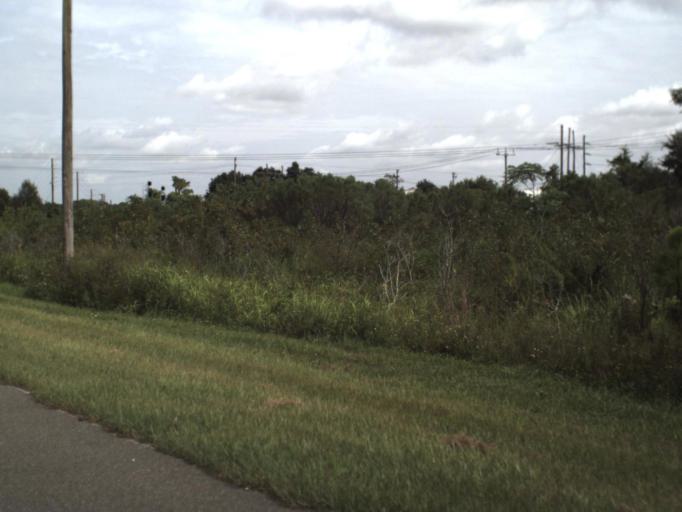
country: US
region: Florida
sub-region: Polk County
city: Auburndale
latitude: 28.0459
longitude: -81.7884
